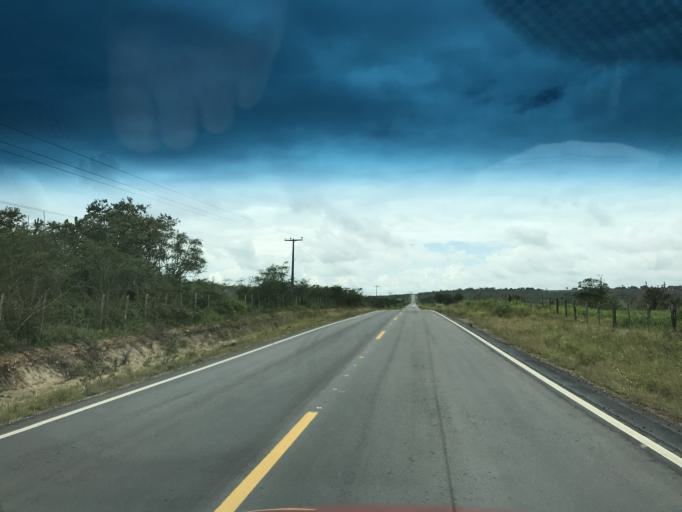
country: BR
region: Bahia
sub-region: Castro Alves
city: Castro Alves
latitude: -12.6753
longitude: -39.2960
